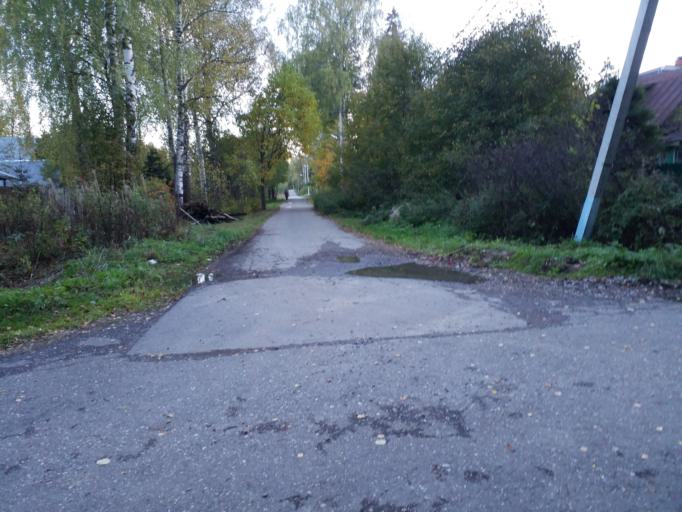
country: RU
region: Moskovskaya
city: Ashukino
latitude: 56.1688
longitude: 37.9579
